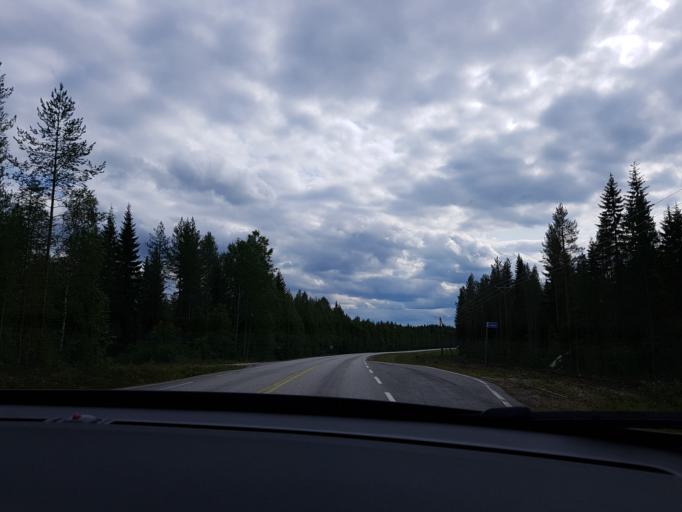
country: FI
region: Kainuu
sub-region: Kehys-Kainuu
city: Kuhmo
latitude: 64.2969
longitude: 29.8527
